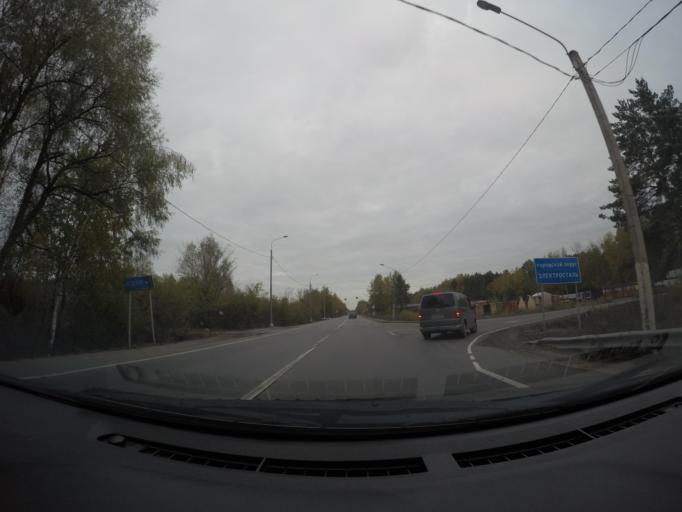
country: RU
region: Moskovskaya
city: Imeni Vorovskogo
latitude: 55.7220
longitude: 38.3740
